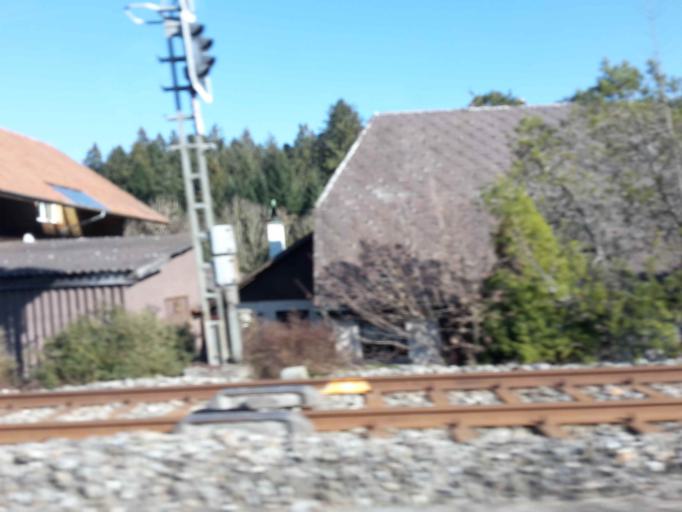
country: CH
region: Bern
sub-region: Emmental District
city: Durrenroth
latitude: 47.0755
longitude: 7.7488
